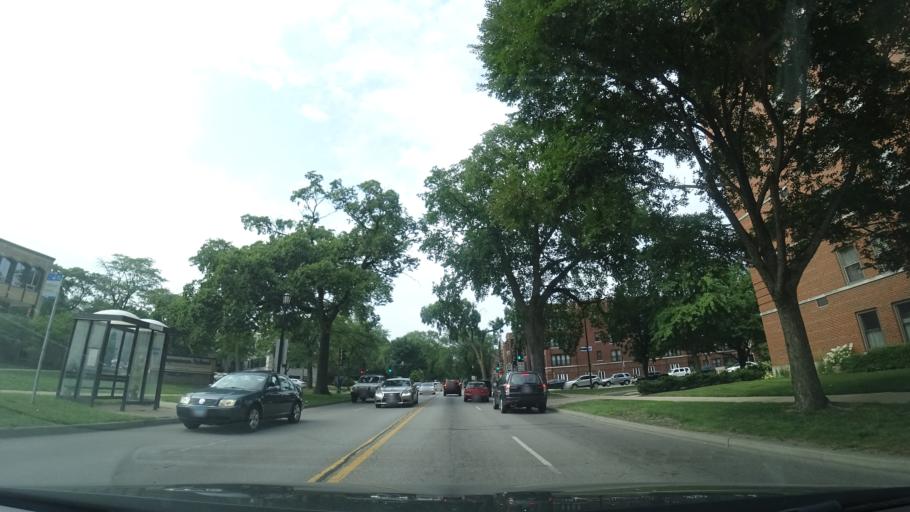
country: US
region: Illinois
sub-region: Cook County
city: Evanston
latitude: 42.0466
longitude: -87.6887
